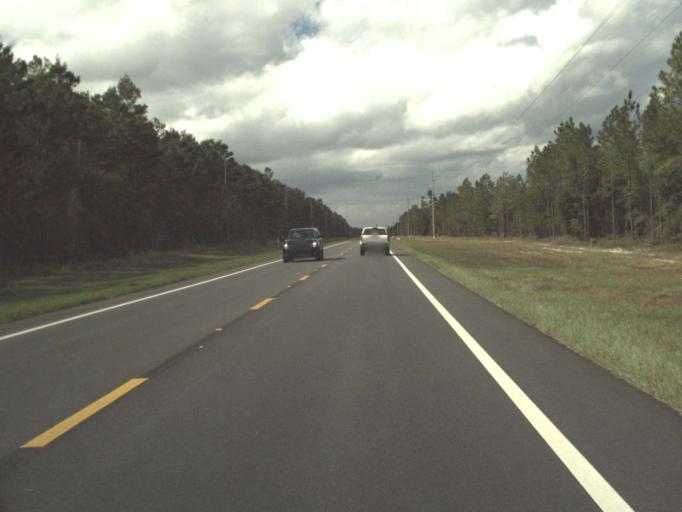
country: US
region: Florida
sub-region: Liberty County
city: Bristol
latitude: 30.4191
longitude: -84.8892
